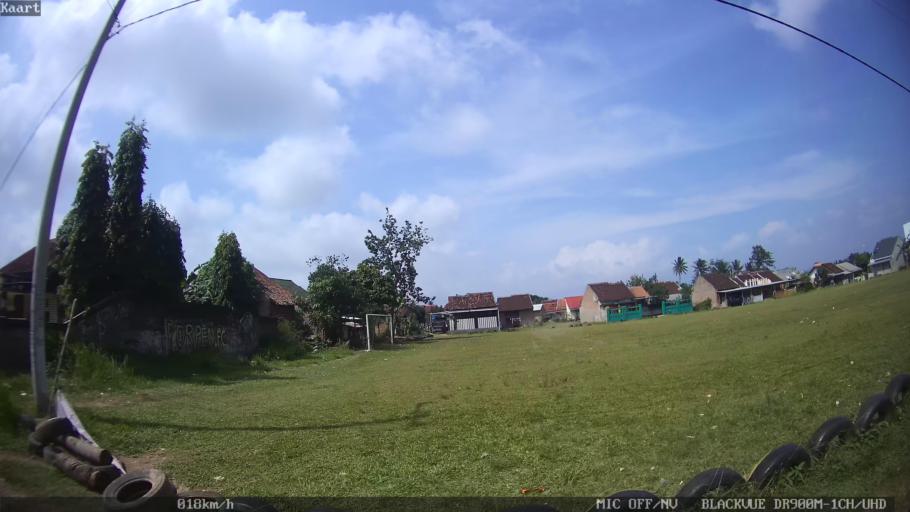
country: ID
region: Lampung
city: Kedaton
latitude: -5.3306
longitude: 105.2814
